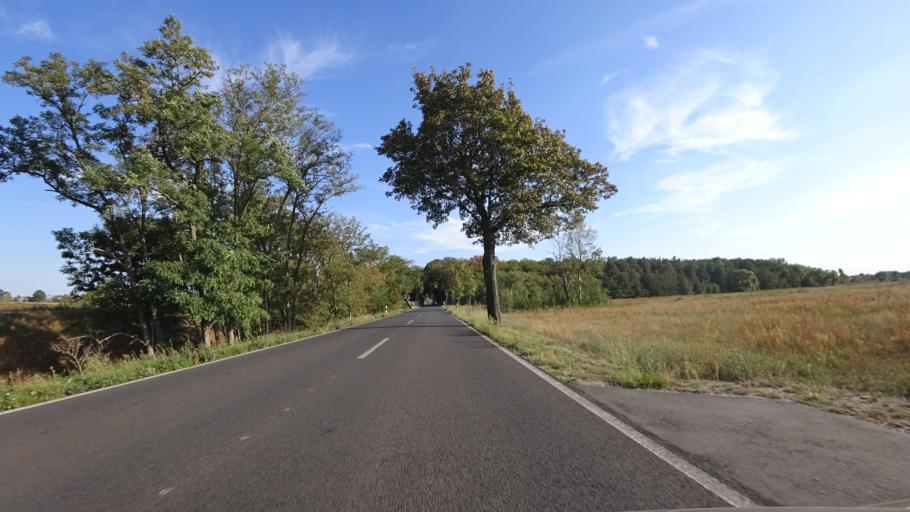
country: DE
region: Brandenburg
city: Stahnsdorf
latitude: 52.3465
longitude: 13.1971
